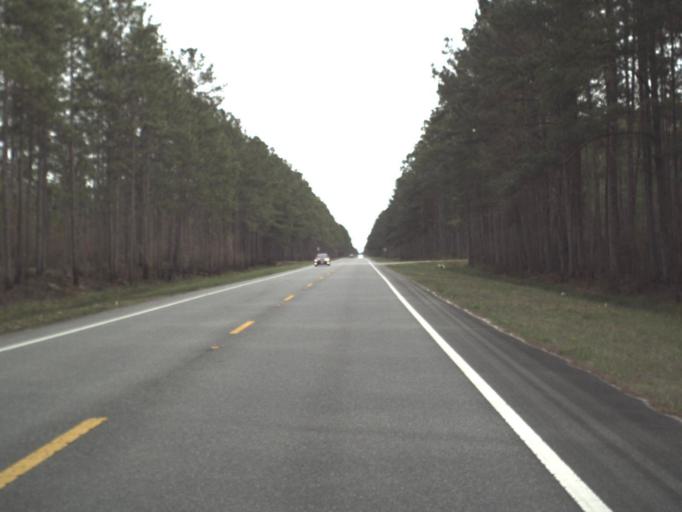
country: US
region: Florida
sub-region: Gadsden County
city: Midway
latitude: 30.3832
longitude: -84.5678
